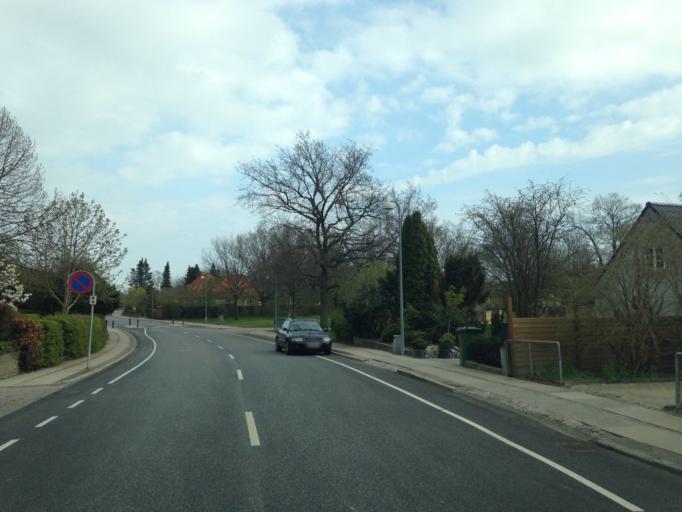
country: DK
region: Capital Region
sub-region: Hoje-Taastrup Kommune
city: Taastrup
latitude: 55.6254
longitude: 12.2991
